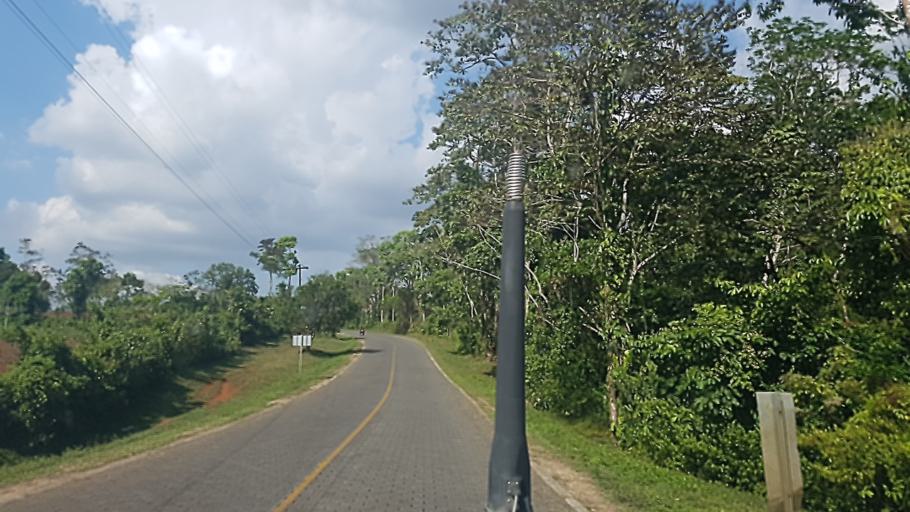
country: NI
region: Atlantico Sur
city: Nueva Guinea
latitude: 11.7052
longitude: -84.3698
